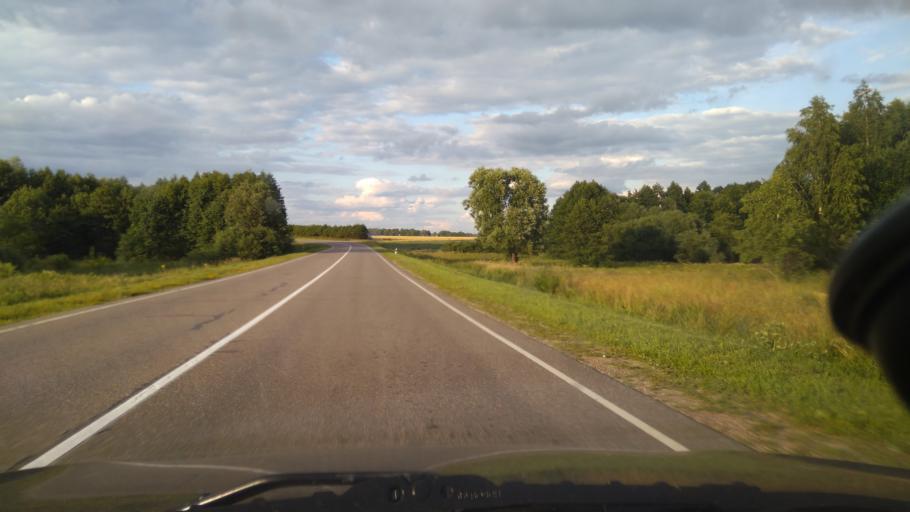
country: BY
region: Grodnenskaya
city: Shchuchin
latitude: 53.5144
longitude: 24.6945
